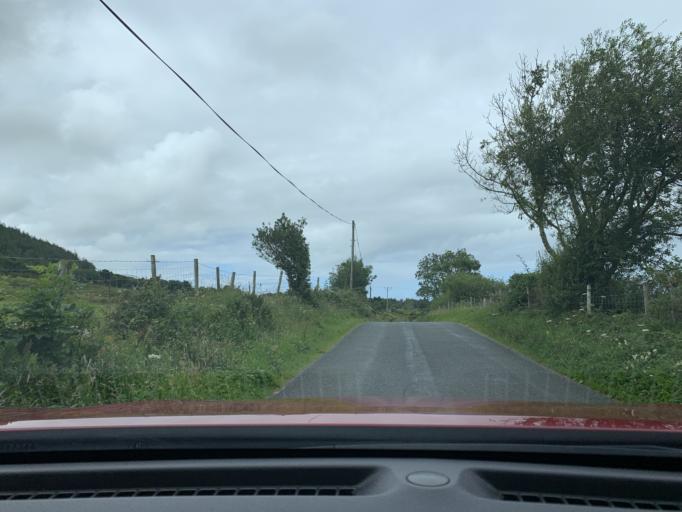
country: IE
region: Connaught
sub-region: County Leitrim
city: Kinlough
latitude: 54.3999
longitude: -8.4137
